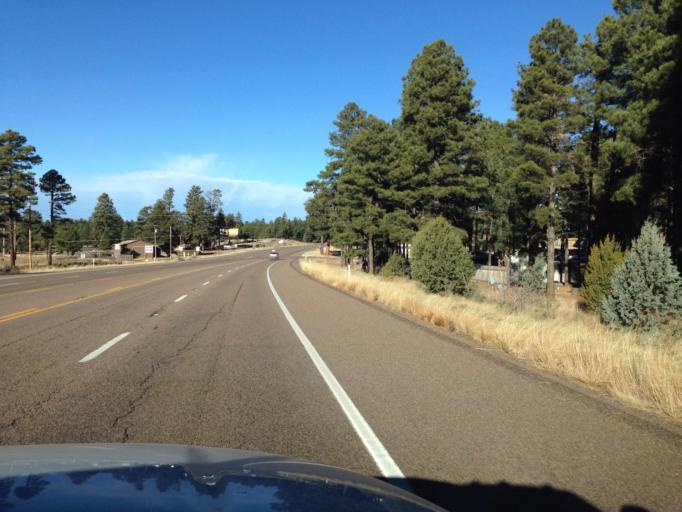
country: US
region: Arizona
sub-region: Navajo County
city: Heber-Overgaard
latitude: 34.3900
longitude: -110.5507
